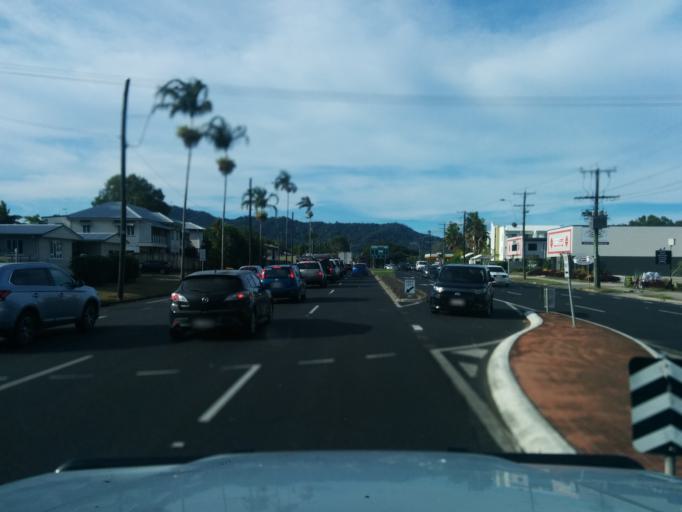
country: AU
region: Queensland
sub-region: Cairns
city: Cairns
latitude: -16.9210
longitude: 145.7402
